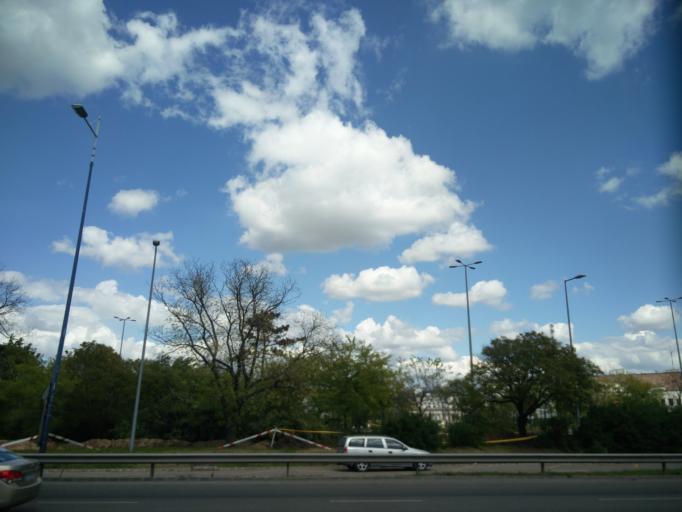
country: HU
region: Budapest
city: Budapest XVIII. keruelet
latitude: 47.4392
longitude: 19.2214
